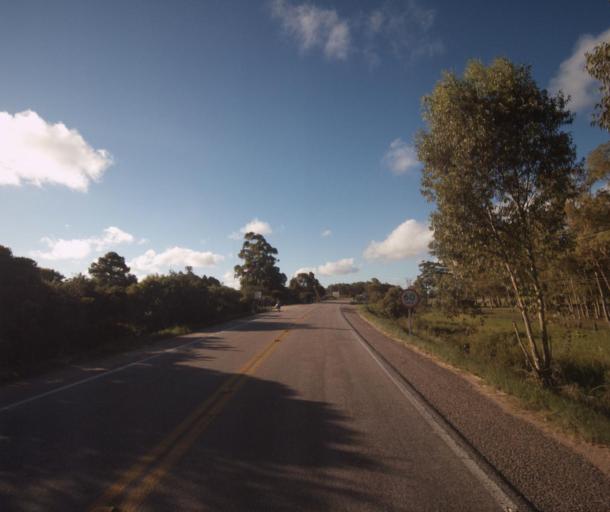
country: BR
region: Rio Grande do Sul
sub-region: Arroio Grande
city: Arroio Grande
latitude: -32.4949
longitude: -52.5799
